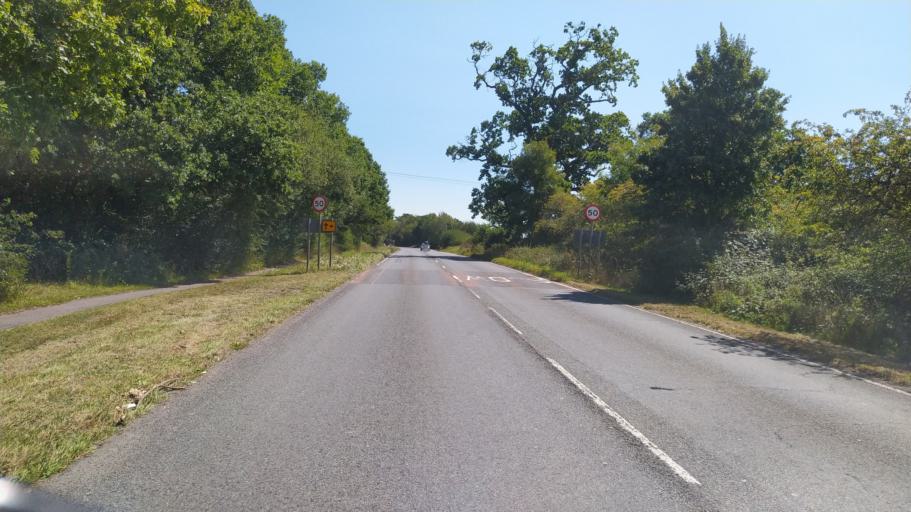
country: GB
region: England
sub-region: Hampshire
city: Cadnam
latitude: 50.9169
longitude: -1.5619
